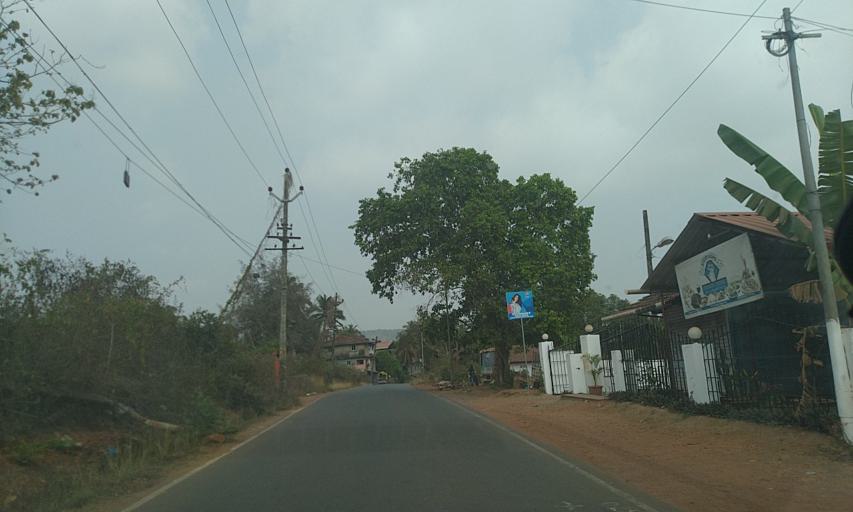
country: IN
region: Goa
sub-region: South Goa
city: Raia
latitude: 15.3079
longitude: 73.9550
